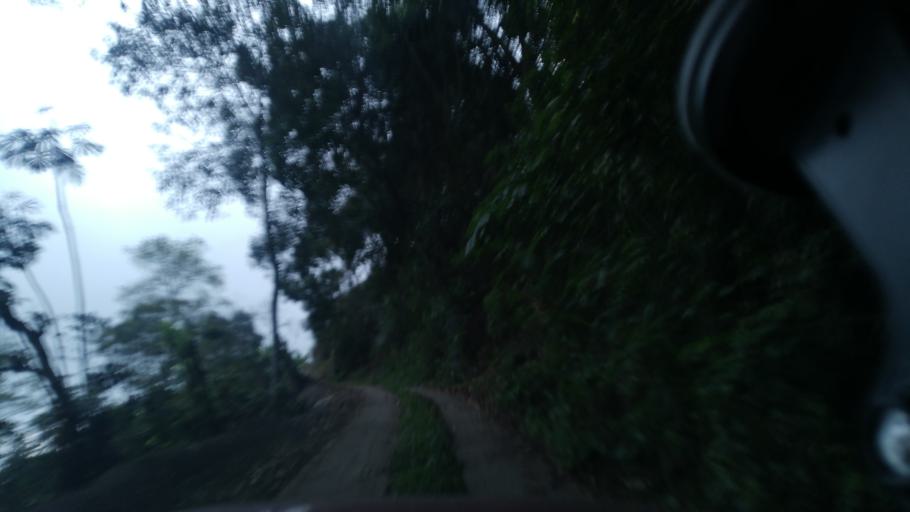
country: CO
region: Cundinamarca
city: San Antonio del Tequendama
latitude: 4.6667
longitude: -74.3992
